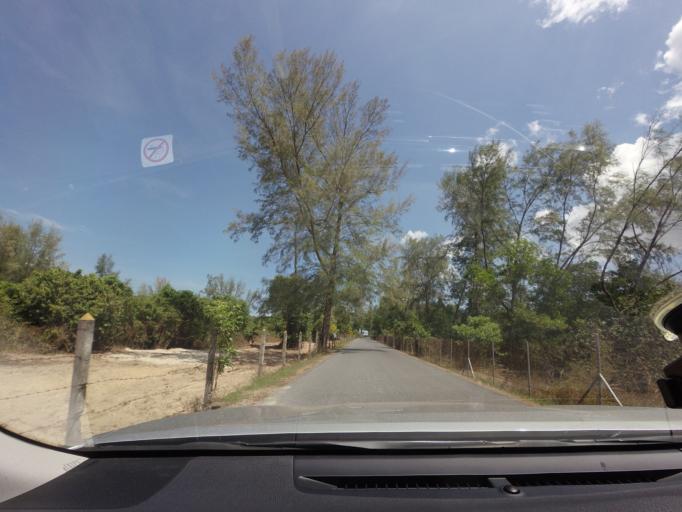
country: TH
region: Phuket
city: Thalang
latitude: 8.0333
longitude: 98.2918
